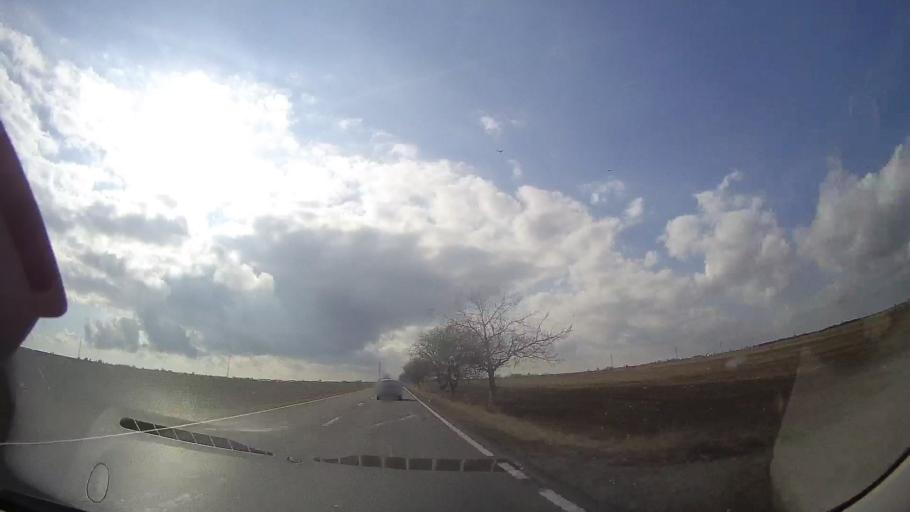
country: RO
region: Constanta
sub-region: Comuna Agigea
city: Agigea
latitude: 44.0778
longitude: 28.6015
